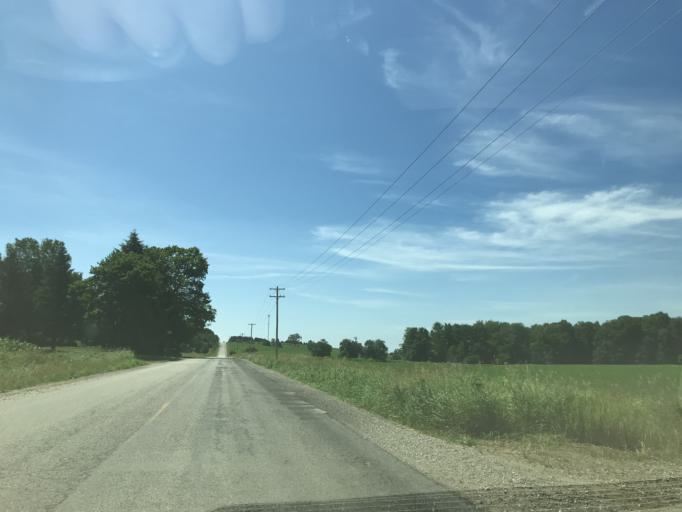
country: US
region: Michigan
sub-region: Missaukee County
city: Lake City
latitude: 44.3048
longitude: -85.0746
